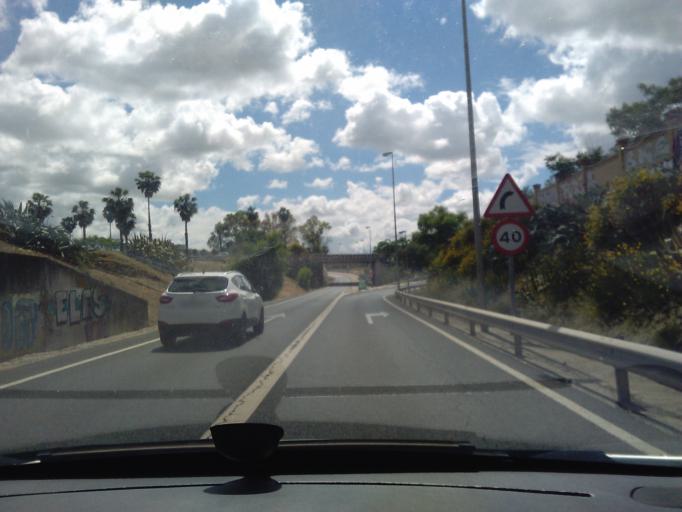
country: ES
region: Andalusia
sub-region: Provincia de Sevilla
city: Sevilla
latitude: 37.3421
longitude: -5.9712
